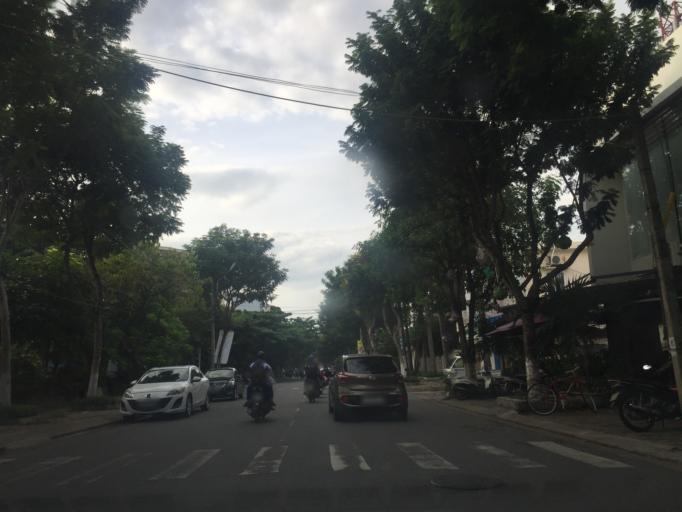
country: VN
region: Da Nang
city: Da Nang
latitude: 16.0797
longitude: 108.2115
